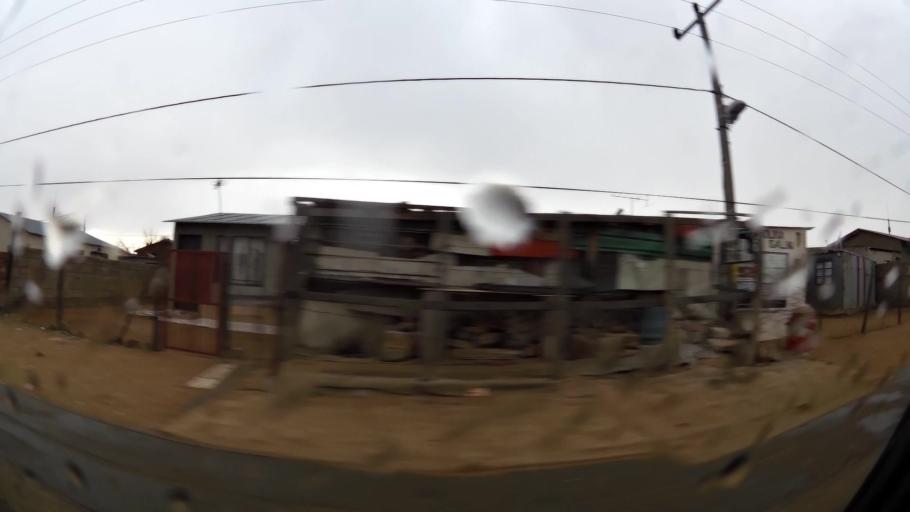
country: ZA
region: Gauteng
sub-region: City of Johannesburg Metropolitan Municipality
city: Roodepoort
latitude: -26.1787
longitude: 27.7883
